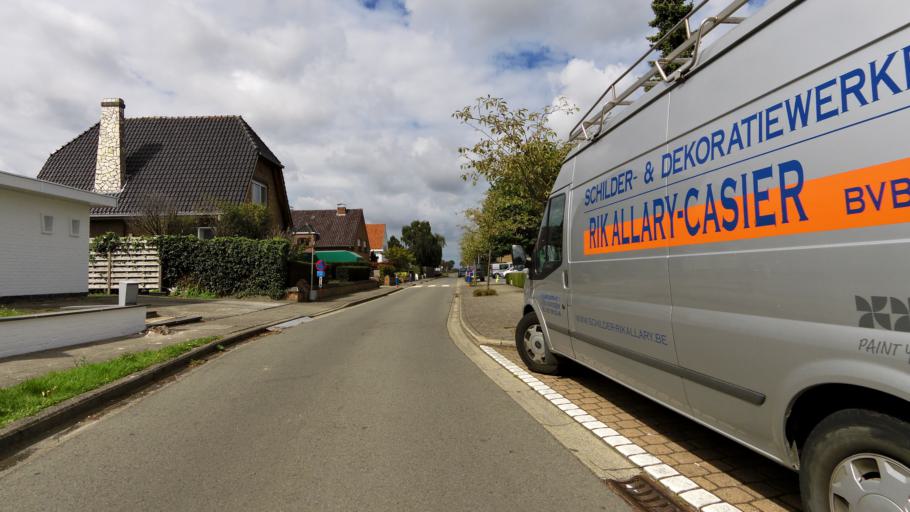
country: BE
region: Flanders
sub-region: Provincie West-Vlaanderen
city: Gistel
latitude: 51.1604
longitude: 2.9698
